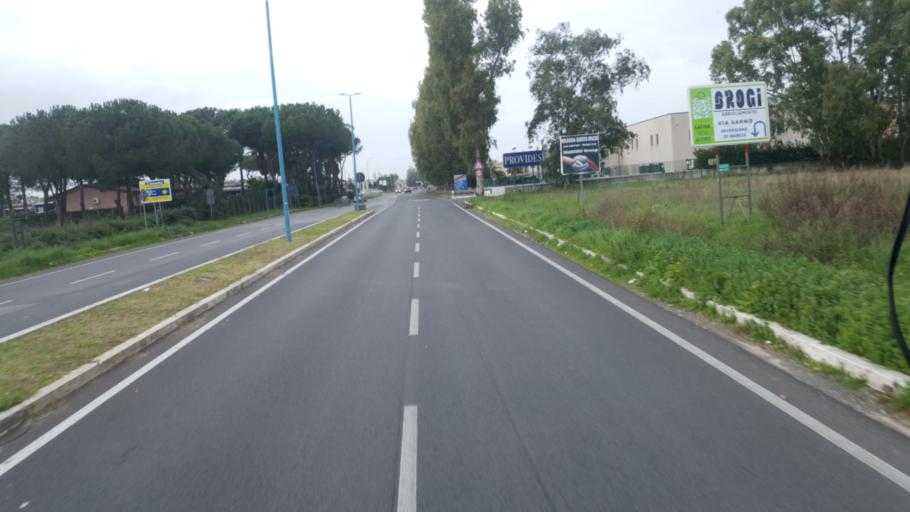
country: IT
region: Latium
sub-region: Provincia di Latina
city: Latina
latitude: 41.4789
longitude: 12.8722
